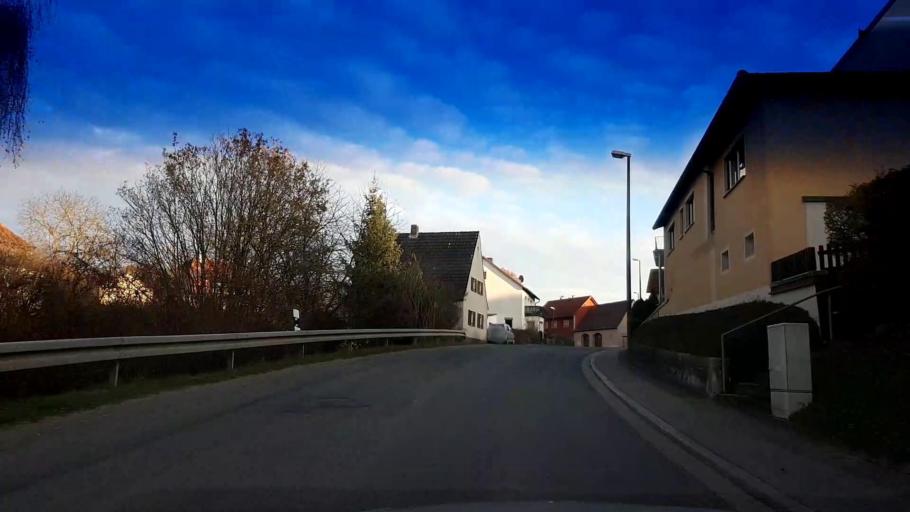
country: DE
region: Bavaria
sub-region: Upper Franconia
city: Priesendorf
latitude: 49.8829
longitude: 10.7270
